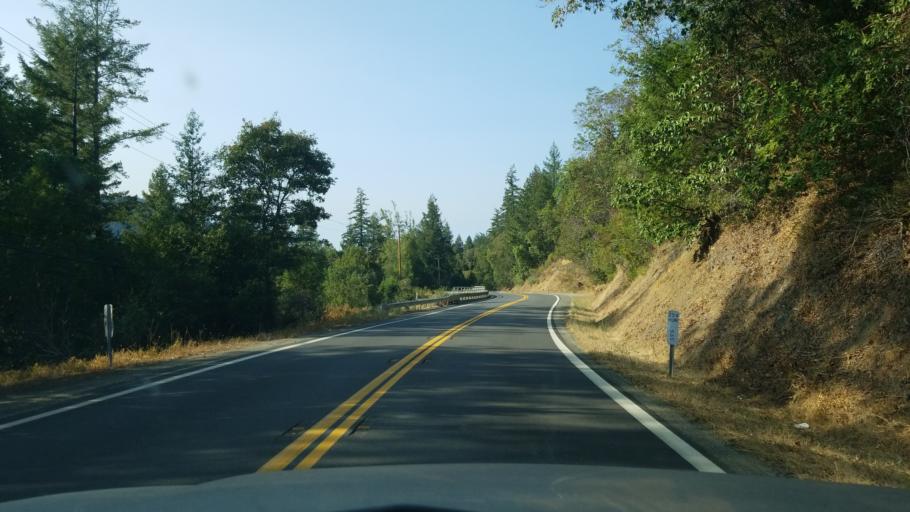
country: US
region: California
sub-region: Humboldt County
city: Redway
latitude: 40.2239
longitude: -123.8213
